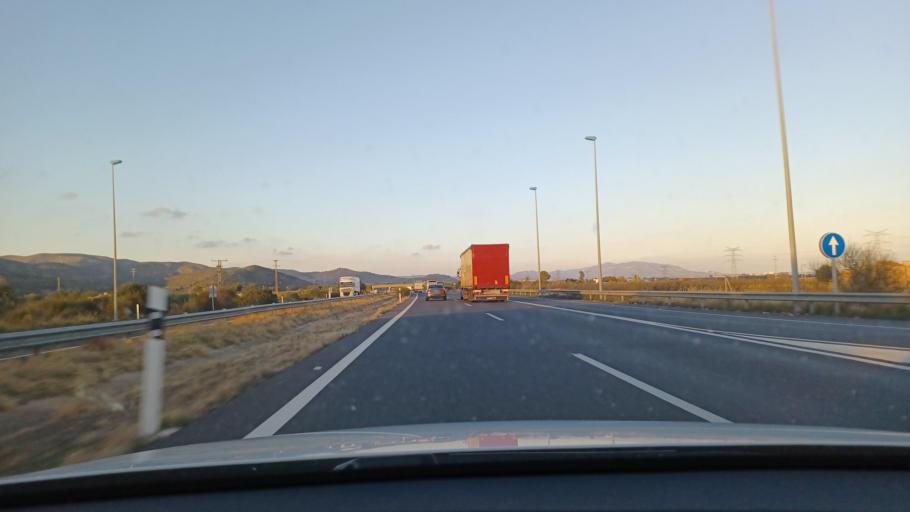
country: ES
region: Valencia
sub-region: Provincia de Castello
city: Orpesa/Oropesa del Mar
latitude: 40.1339
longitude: 0.1412
